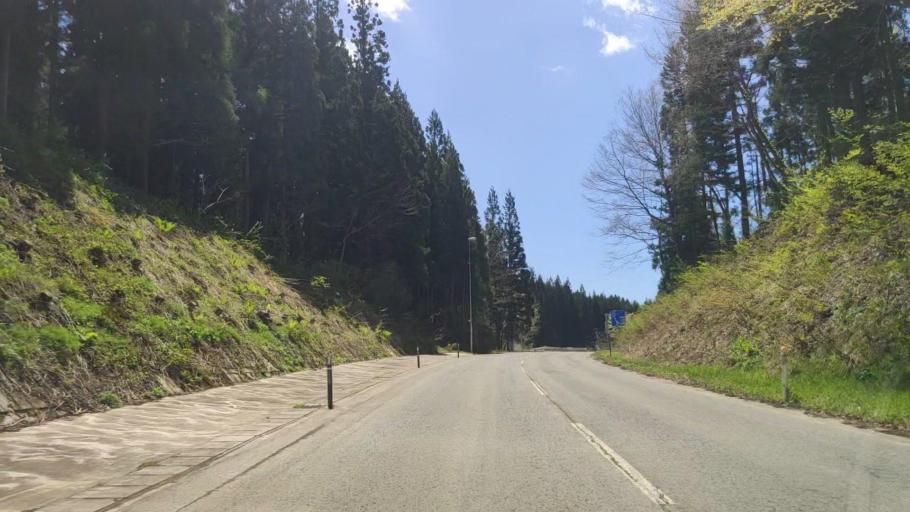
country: JP
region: Yamagata
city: Shinjo
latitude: 38.9192
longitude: 140.3288
